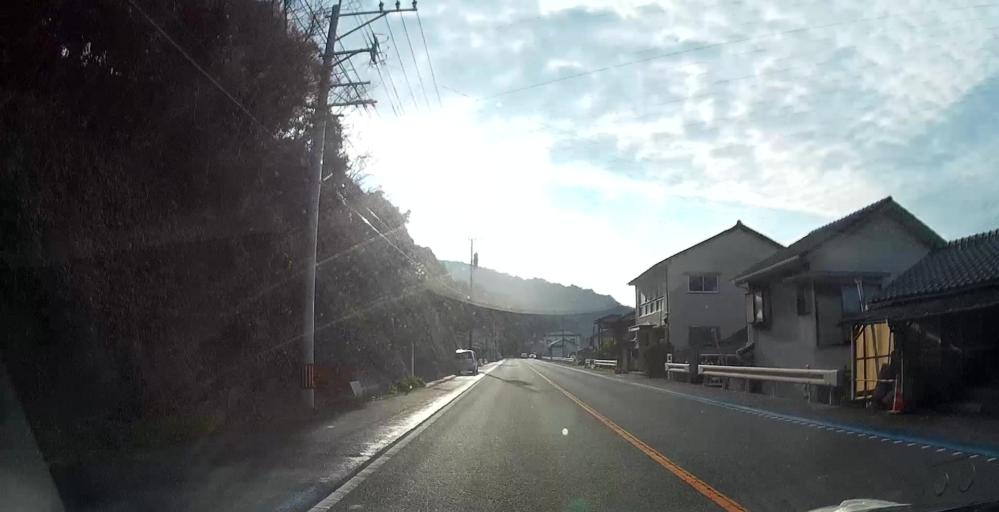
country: JP
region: Kumamoto
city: Matsubase
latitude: 32.6565
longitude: 130.5127
